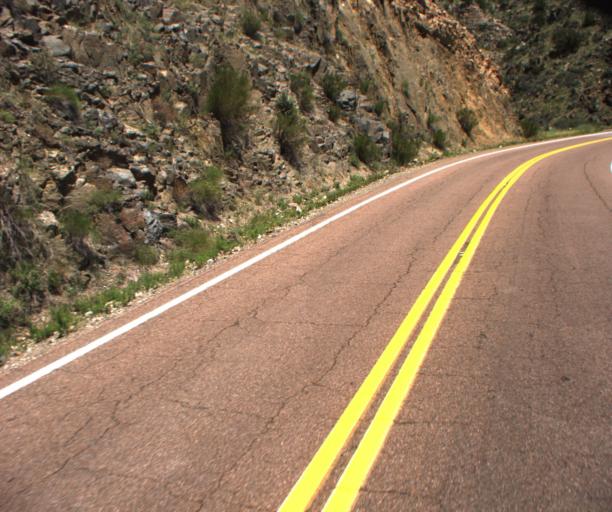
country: US
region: Arizona
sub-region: Navajo County
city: Cibecue
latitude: 33.8059
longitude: -110.4855
